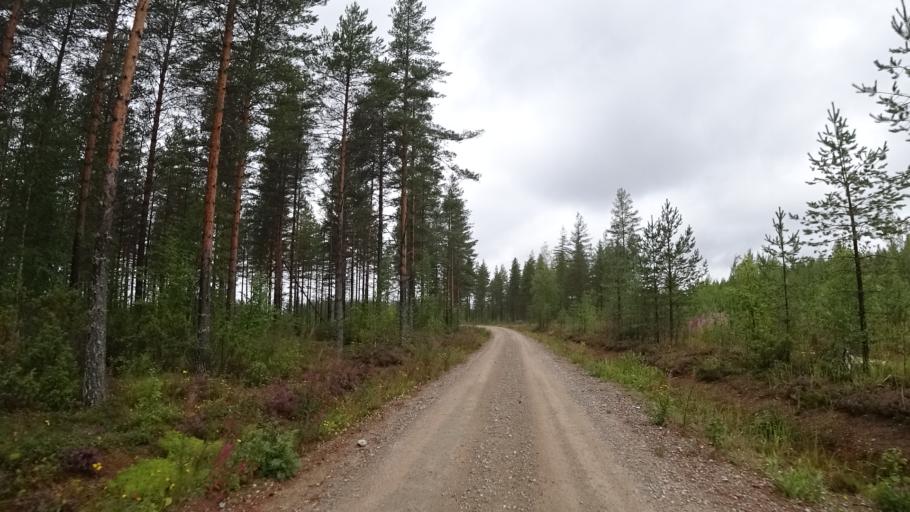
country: FI
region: North Karelia
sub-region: Pielisen Karjala
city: Lieksa
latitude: 63.5186
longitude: 30.1137
